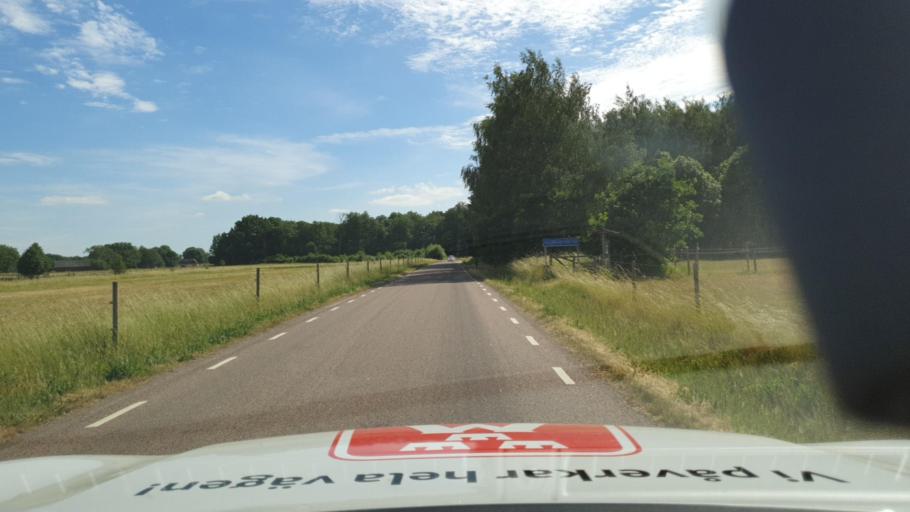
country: SE
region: Skane
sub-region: Sjobo Kommun
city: Blentarp
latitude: 55.6149
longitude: 13.6191
